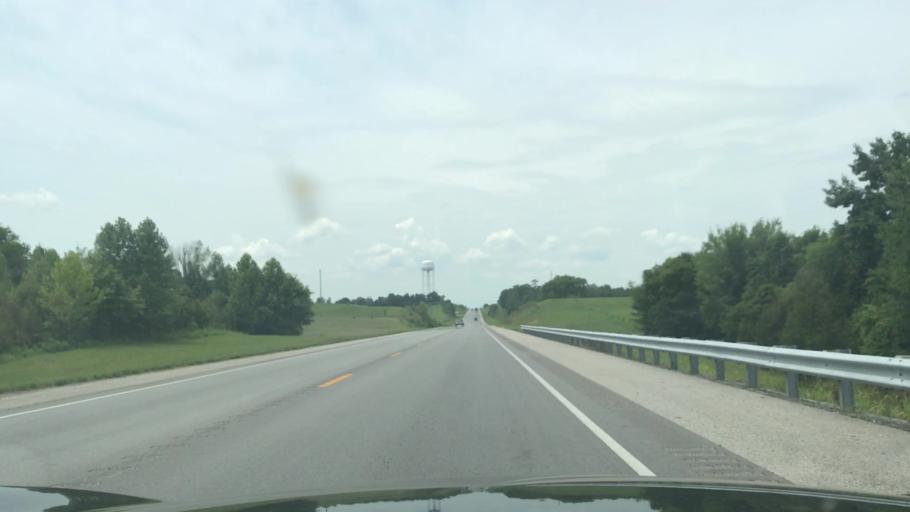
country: US
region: Kentucky
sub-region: Taylor County
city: Campbellsville
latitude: 37.3131
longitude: -85.4239
